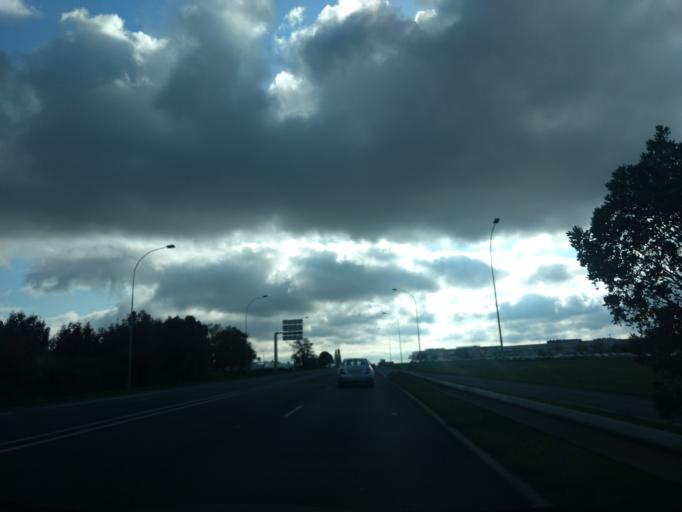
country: FR
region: Poitou-Charentes
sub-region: Departement de la Vienne
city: Chasseneuil-du-Poitou
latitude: 46.6588
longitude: 0.3681
